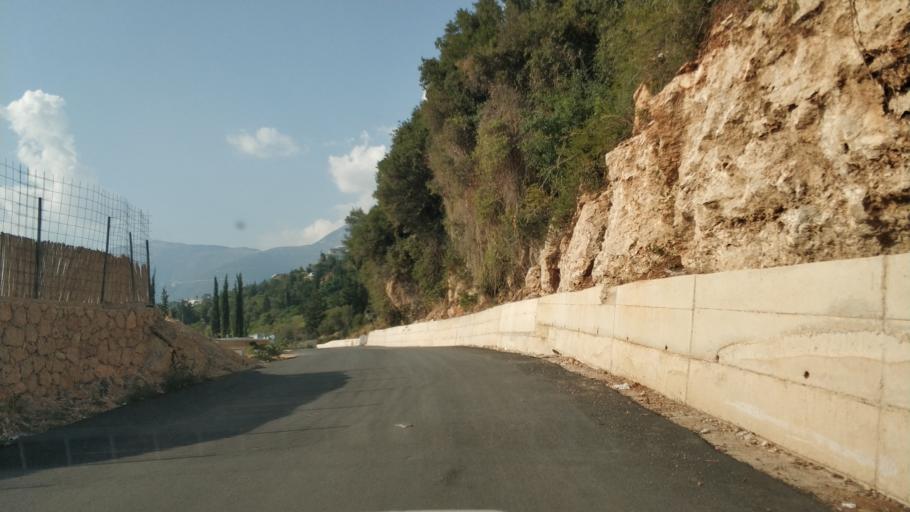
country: AL
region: Vlore
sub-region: Rrethi i Vlores
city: Vranisht
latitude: 40.1413
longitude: 19.6419
